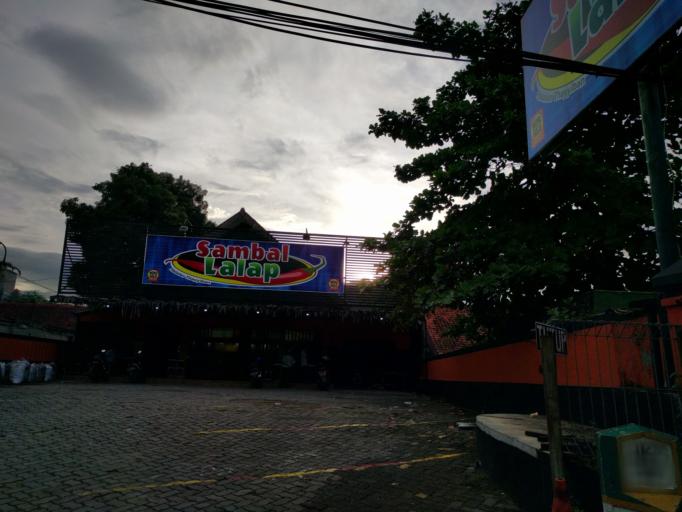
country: ID
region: West Java
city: Bogor
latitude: -6.5806
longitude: 106.7967
